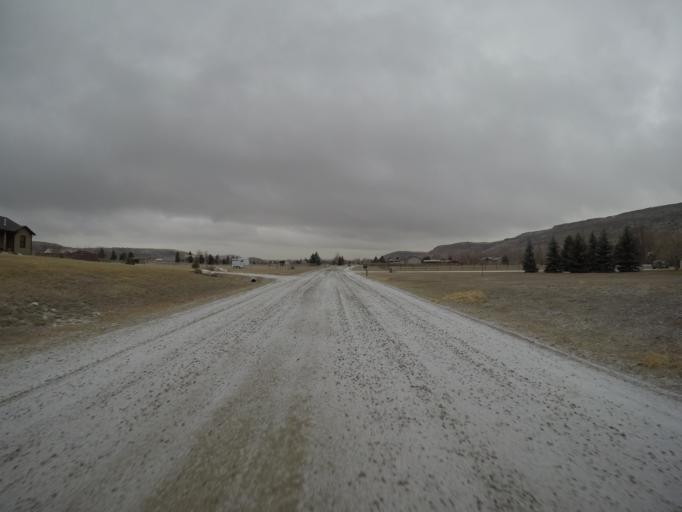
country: US
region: Montana
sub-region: Stillwater County
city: Absarokee
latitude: 45.5331
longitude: -109.4449
